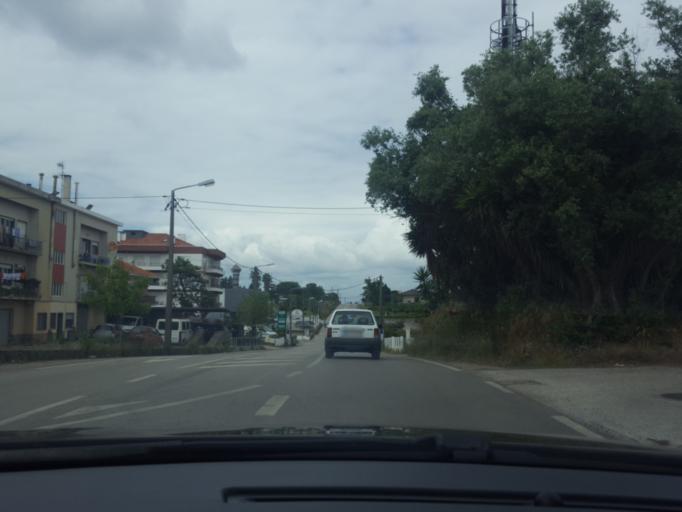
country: PT
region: Leiria
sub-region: Leiria
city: Leiria
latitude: 39.7575
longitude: -8.7867
